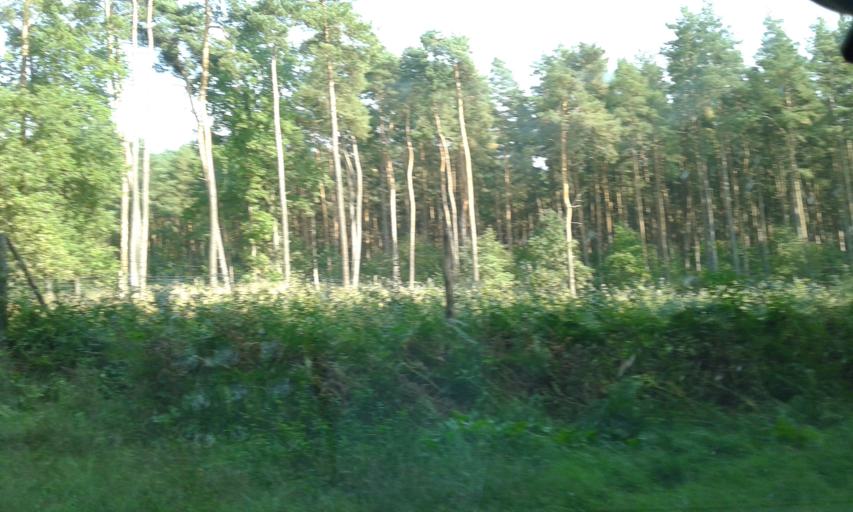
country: PL
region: West Pomeranian Voivodeship
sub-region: Powiat stargardzki
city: Suchan
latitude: 53.2431
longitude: 15.3618
